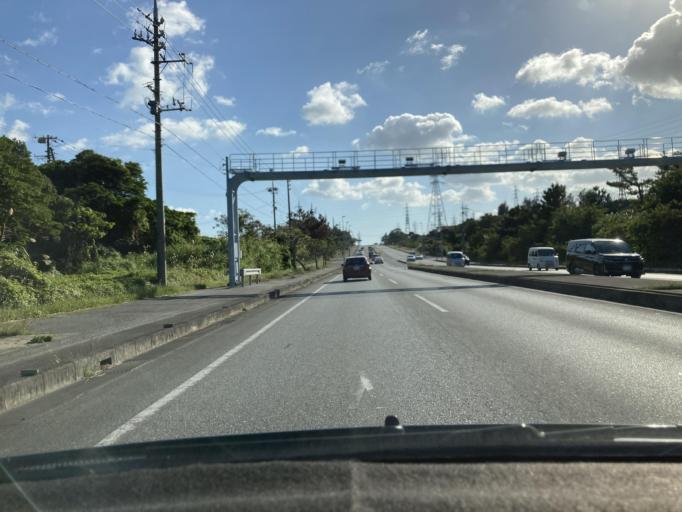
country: JP
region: Okinawa
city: Ishikawa
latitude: 26.3977
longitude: 127.8290
